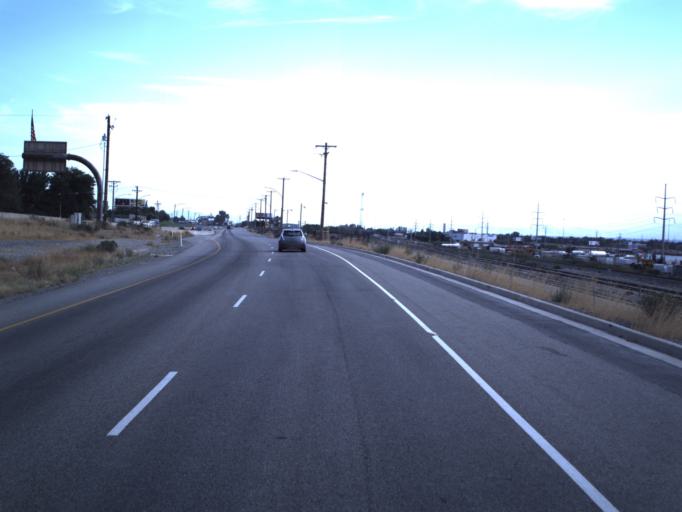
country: US
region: Utah
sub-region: Davis County
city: North Salt Lake
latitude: 40.8145
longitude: -111.9191
